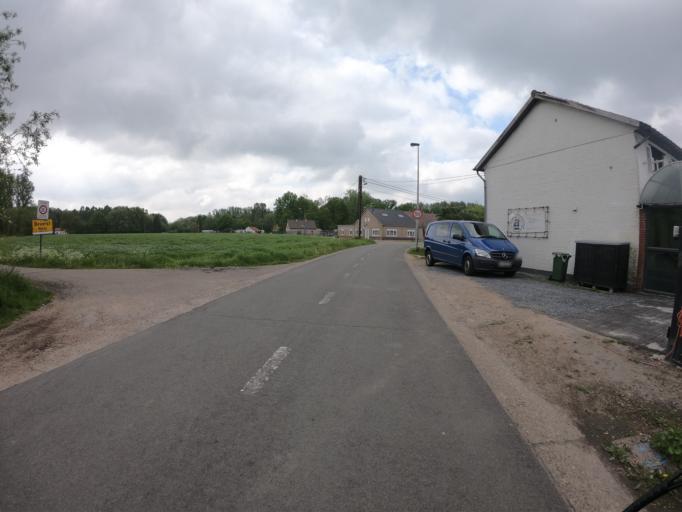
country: BE
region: Flanders
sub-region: Provincie Limburg
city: Diepenbeek
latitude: 50.9052
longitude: 5.4524
